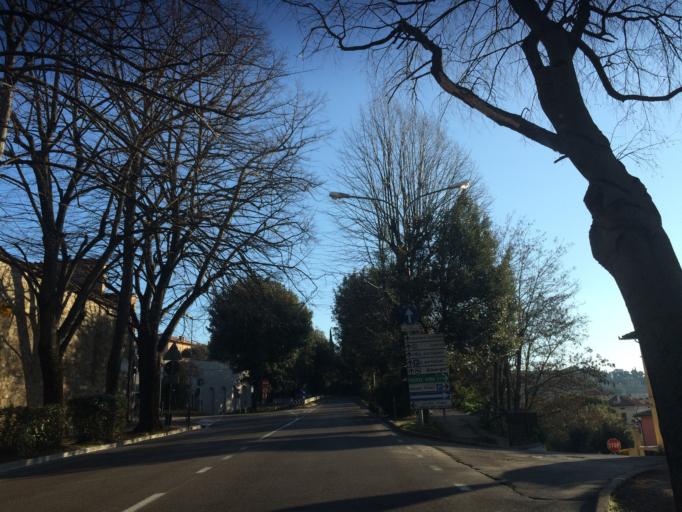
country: IT
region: Umbria
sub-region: Provincia di Perugia
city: Perugia
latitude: 43.1031
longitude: 12.3859
